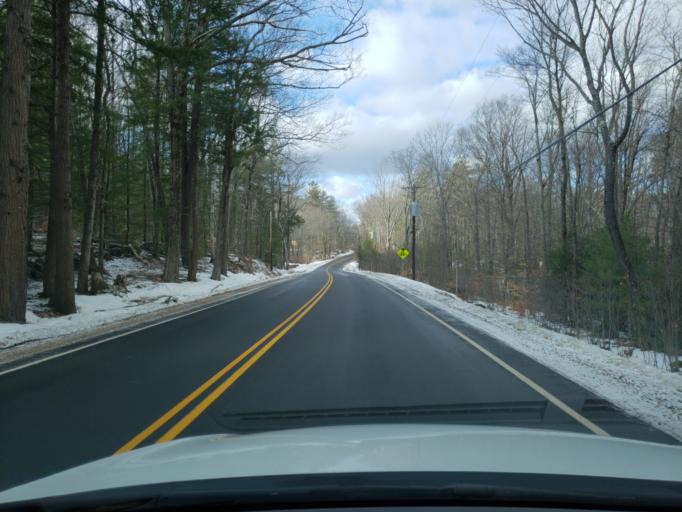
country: US
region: New Hampshire
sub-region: Hillsborough County
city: Deering
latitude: 43.0093
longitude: -71.8404
